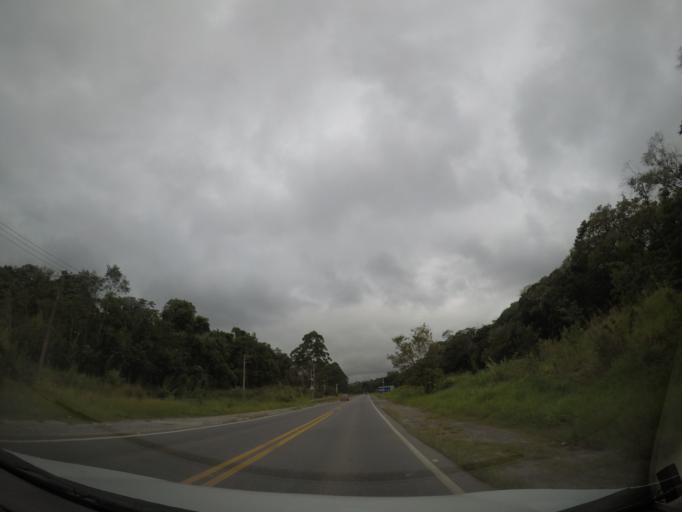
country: BR
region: Sao Paulo
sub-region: Aruja
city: Aruja
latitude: -23.3779
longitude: -46.4339
